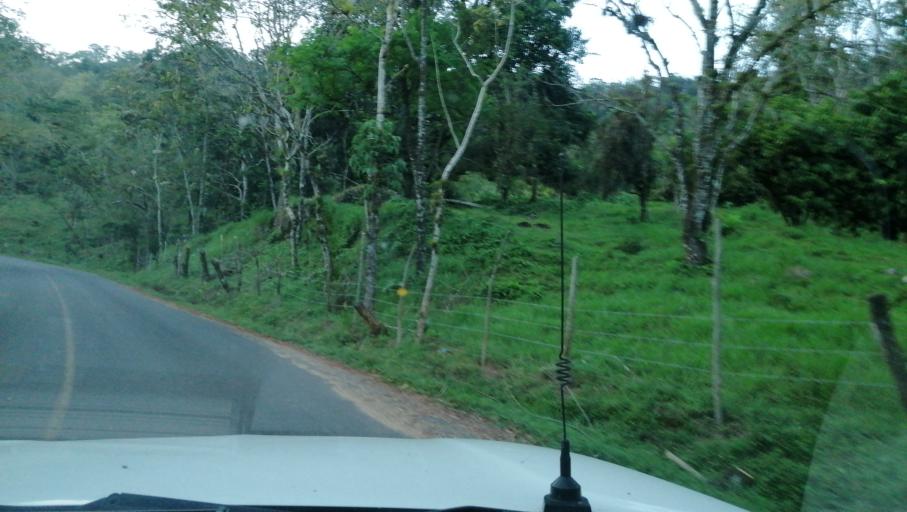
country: MX
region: Chiapas
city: Ostuacan
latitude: 17.4254
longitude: -93.3393
